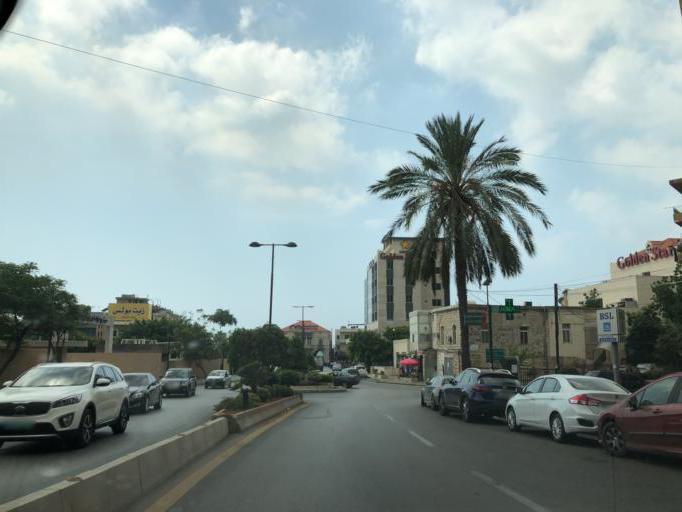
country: LB
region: Mont-Liban
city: Djounie
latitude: 33.9875
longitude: 35.6392
